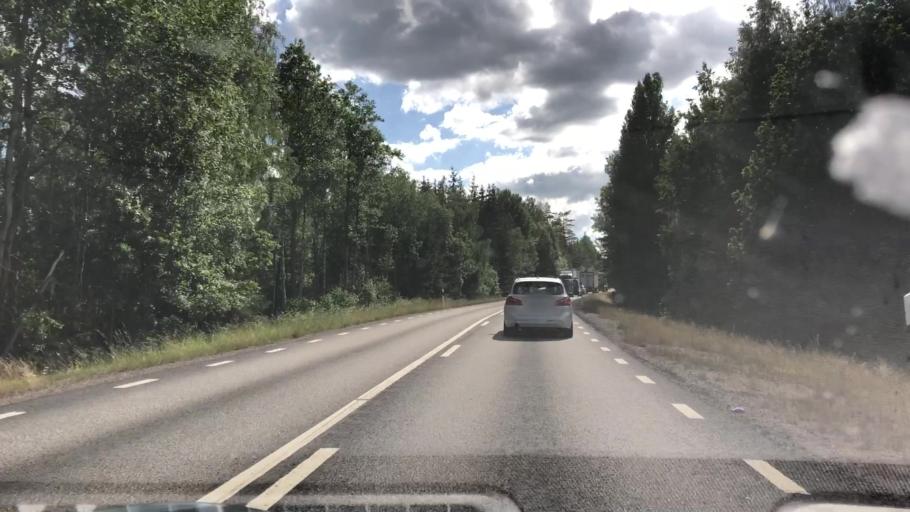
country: SE
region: Kalmar
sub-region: Hultsfreds Kommun
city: Virserum
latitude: 57.3014
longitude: 15.5791
